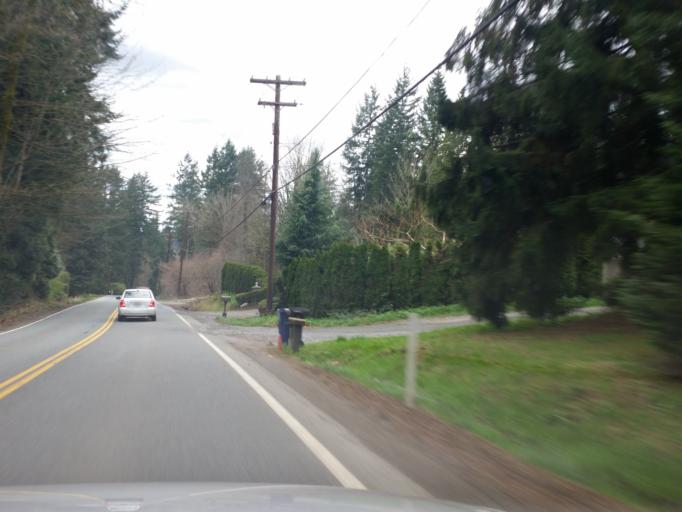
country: US
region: Washington
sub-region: Snohomish County
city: Maltby
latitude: 47.8051
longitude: -122.1317
